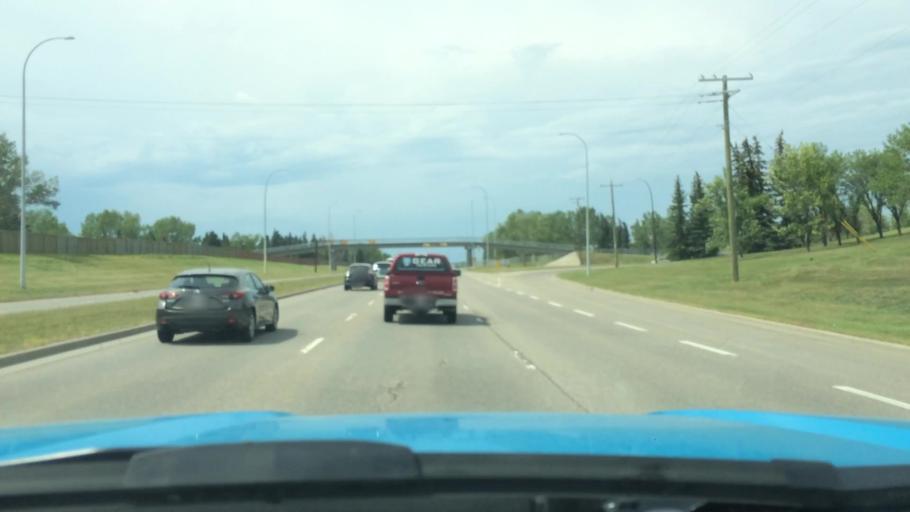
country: CA
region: Alberta
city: Calgary
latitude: 51.1116
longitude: -114.1459
